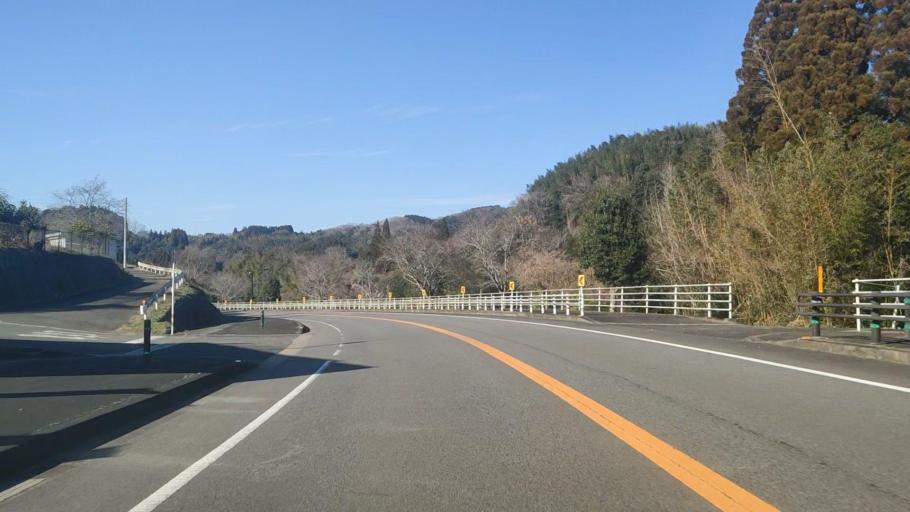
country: JP
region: Oita
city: Usuki
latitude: 33.0595
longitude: 131.6732
